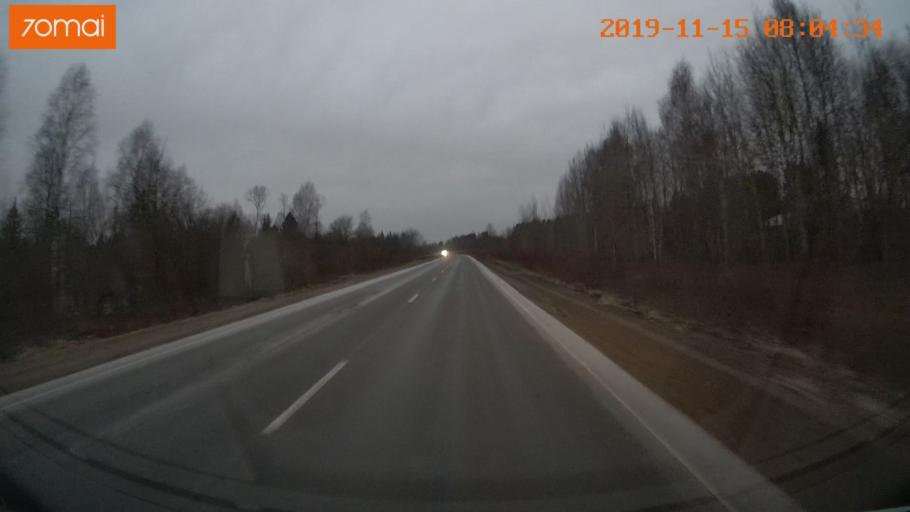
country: RU
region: Vologda
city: Cherepovets
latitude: 59.0095
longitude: 38.0738
